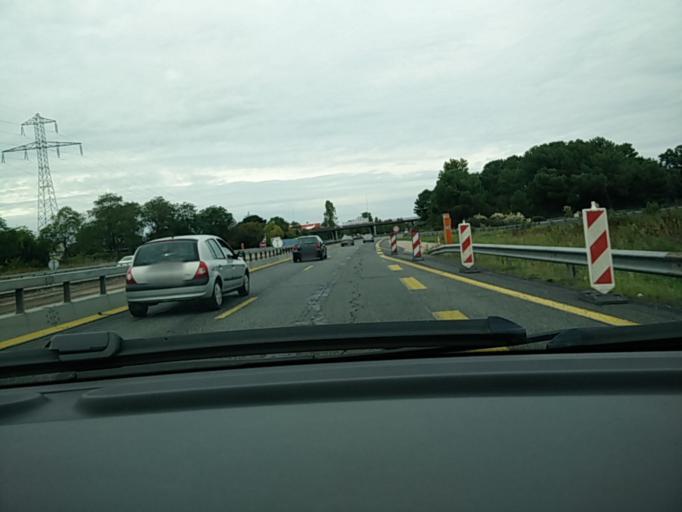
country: FR
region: Aquitaine
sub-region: Departement de la Gironde
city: Le Haillan
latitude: 44.8328
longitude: -0.6763
